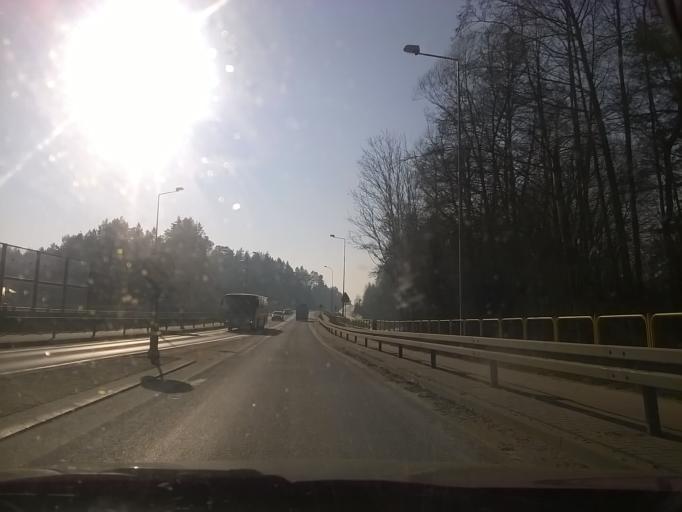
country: PL
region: Warmian-Masurian Voivodeship
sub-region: Powiat olsztynski
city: Barczewo
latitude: 53.8033
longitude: 20.6214
